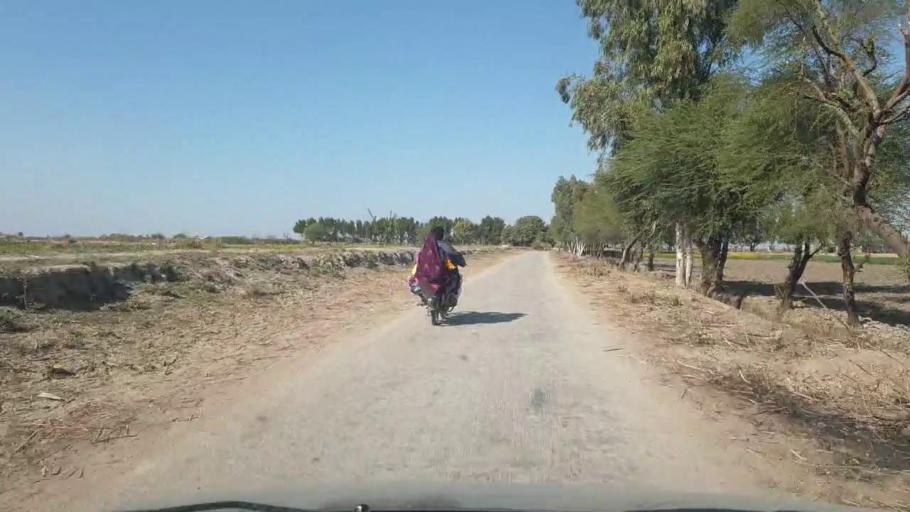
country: PK
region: Sindh
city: Samaro
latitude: 25.3652
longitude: 69.3186
